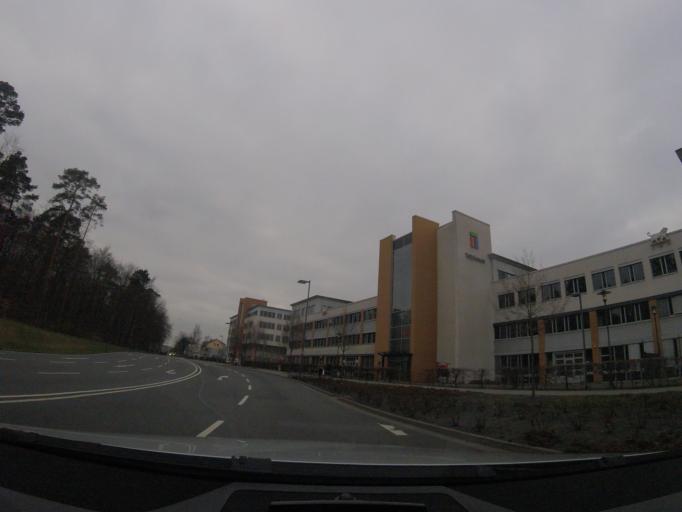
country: DE
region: Hesse
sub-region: Regierungsbezirk Darmstadt
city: Neu Isenburg
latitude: 50.0418
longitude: 8.6836
